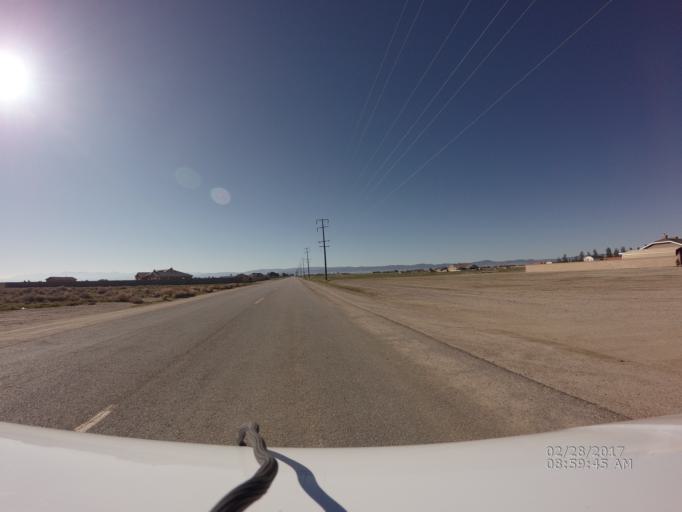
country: US
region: California
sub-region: Kern County
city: Rosamond
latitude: 34.8161
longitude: -118.2553
